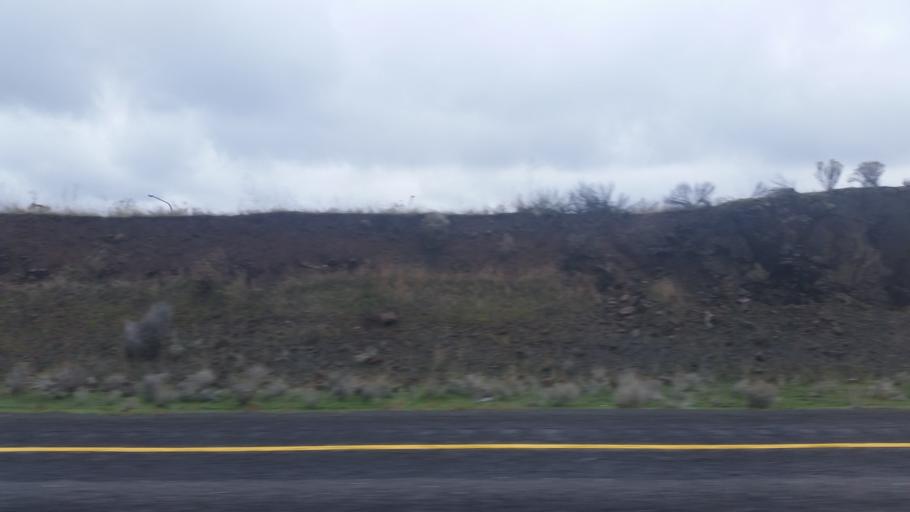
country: US
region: Washington
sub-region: Lincoln County
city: Davenport
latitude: 47.2938
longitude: -118.0321
